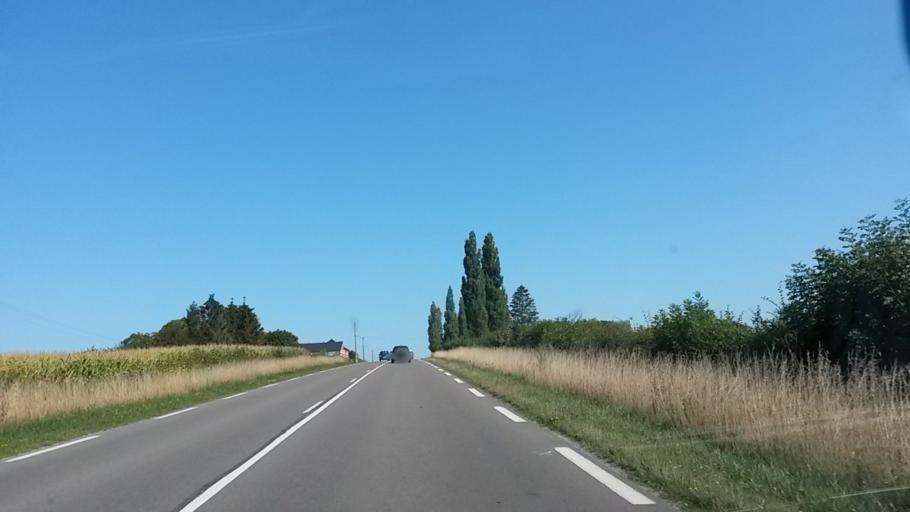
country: FR
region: Nord-Pas-de-Calais
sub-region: Departement du Nord
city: Avesnes-sur-Helpe
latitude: 50.0830
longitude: 3.9297
